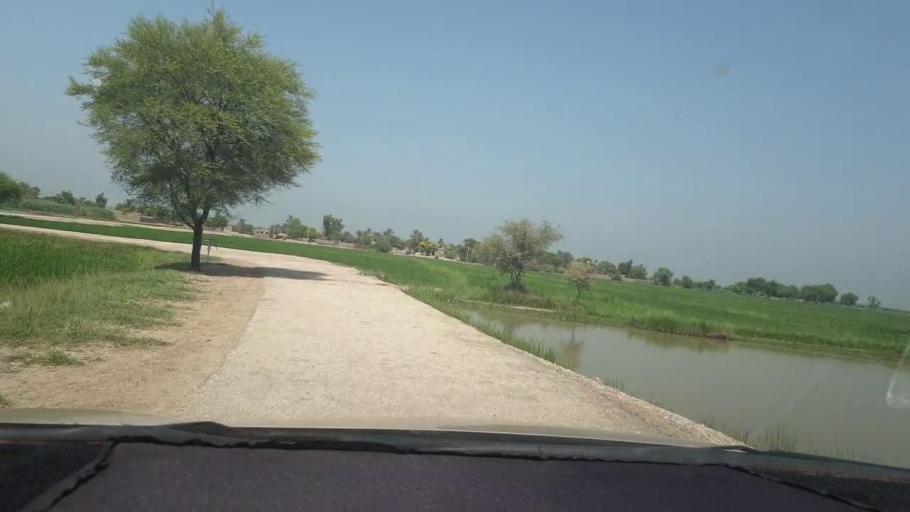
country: PK
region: Sindh
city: Kambar
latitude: 27.6217
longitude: 68.0534
